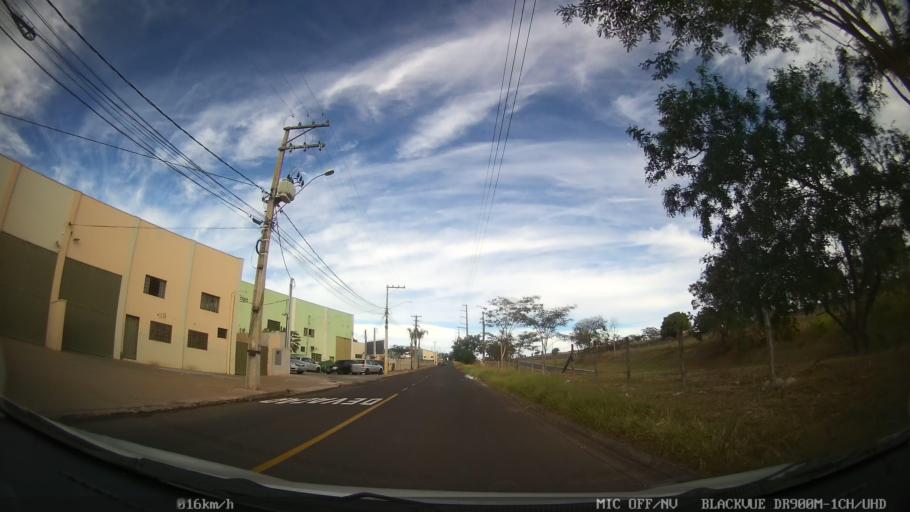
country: BR
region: Sao Paulo
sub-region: Catanduva
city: Catanduva
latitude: -21.1217
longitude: -48.9916
